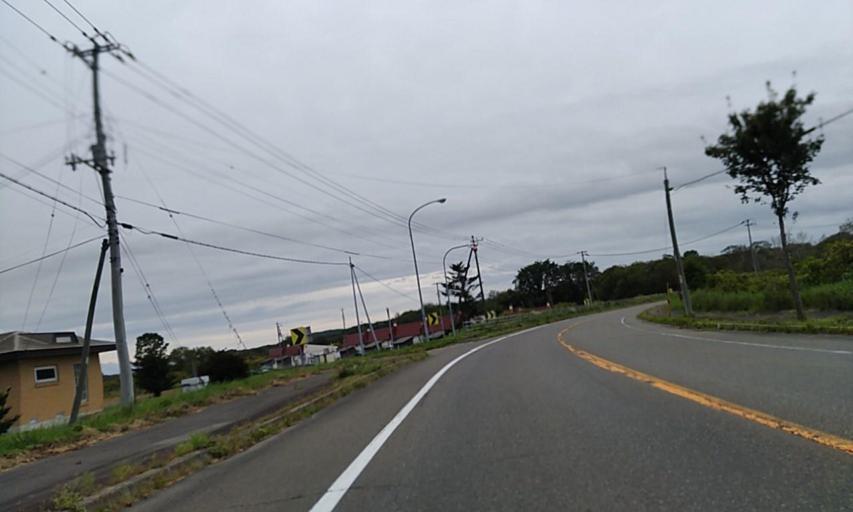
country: JP
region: Hokkaido
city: Obihiro
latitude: 42.4500
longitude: 143.2945
